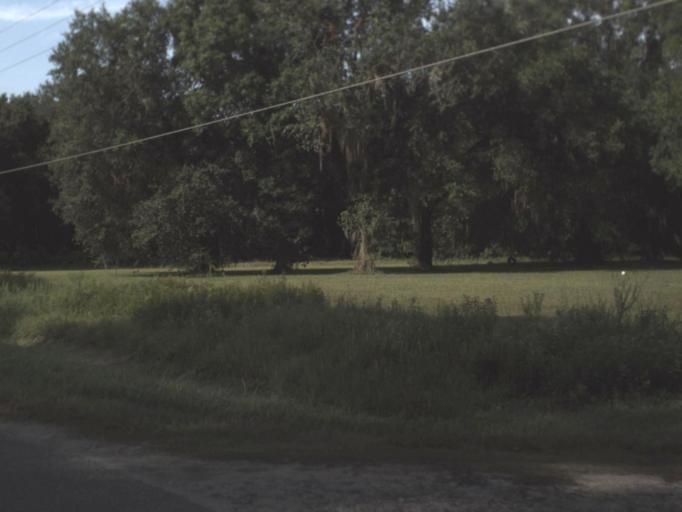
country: US
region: Florida
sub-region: Taylor County
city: Perry
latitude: 30.1688
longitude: -83.5966
